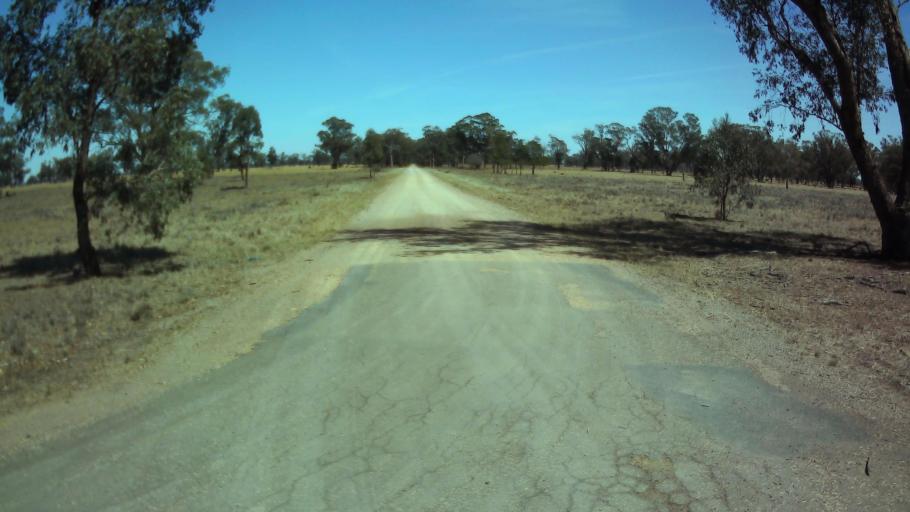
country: AU
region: New South Wales
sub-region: Weddin
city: Grenfell
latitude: -34.0701
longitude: 147.9042
